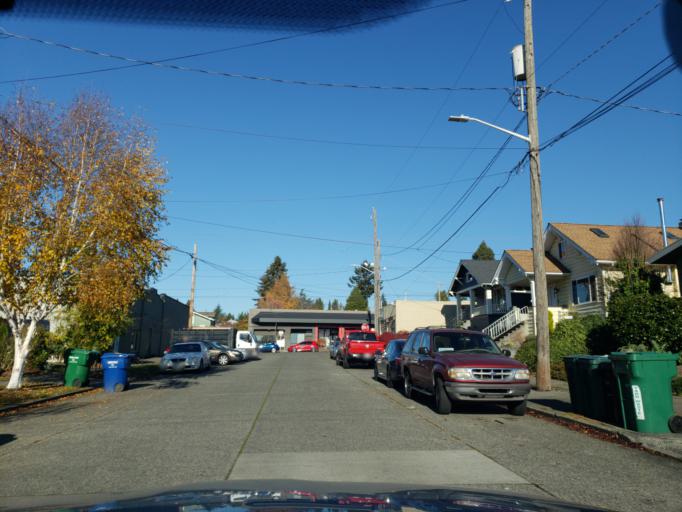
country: US
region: Washington
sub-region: King County
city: Seattle
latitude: 47.6754
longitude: -122.3629
